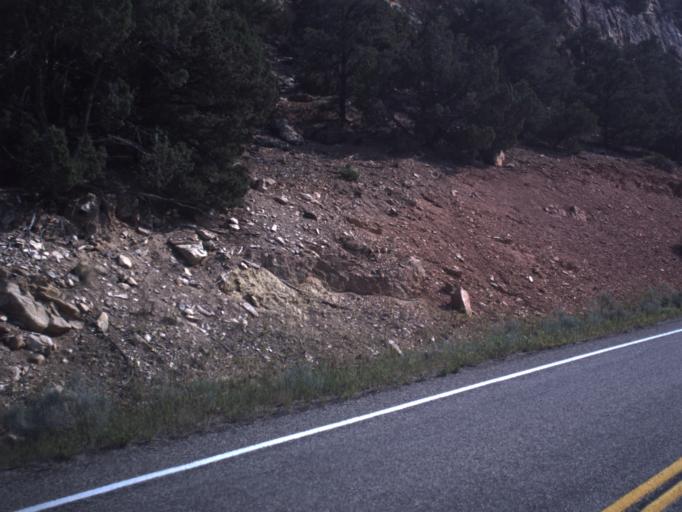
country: US
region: Utah
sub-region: Daggett County
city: Manila
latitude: 40.9532
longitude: -109.4531
